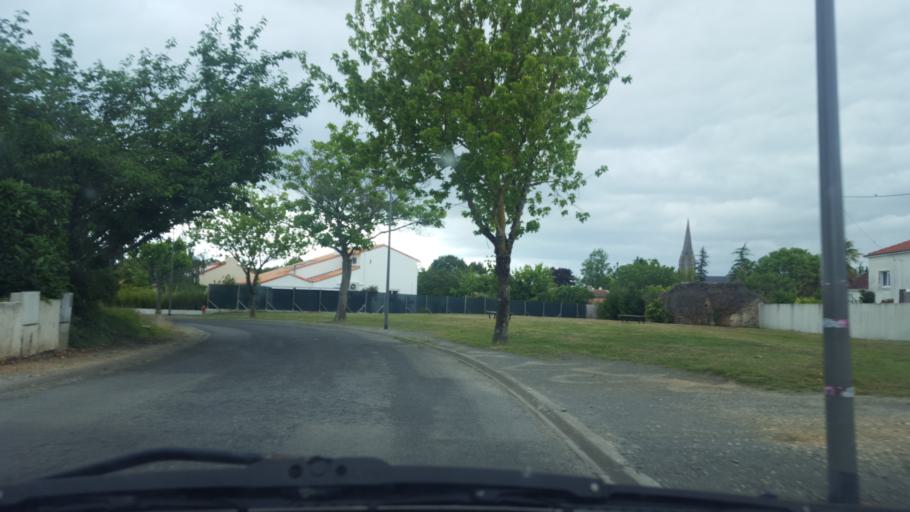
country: FR
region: Pays de la Loire
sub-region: Departement de la Loire-Atlantique
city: Saint-Philbert-de-Grand-Lieu
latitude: 47.0323
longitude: -1.6436
